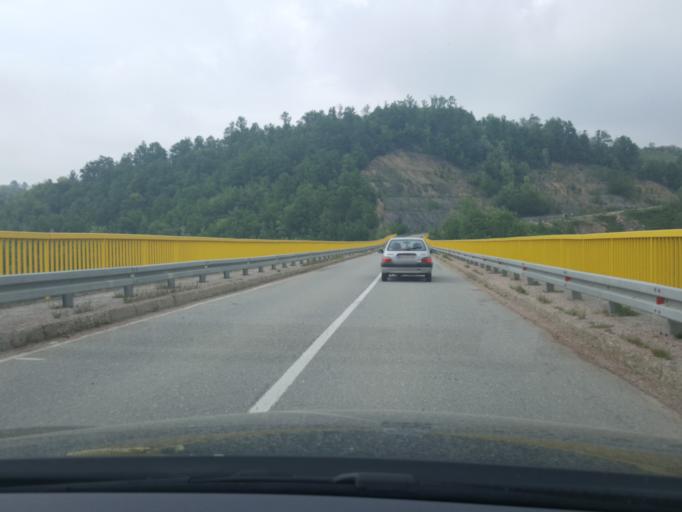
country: RS
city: Kamenica
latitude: 44.2401
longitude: 19.7208
